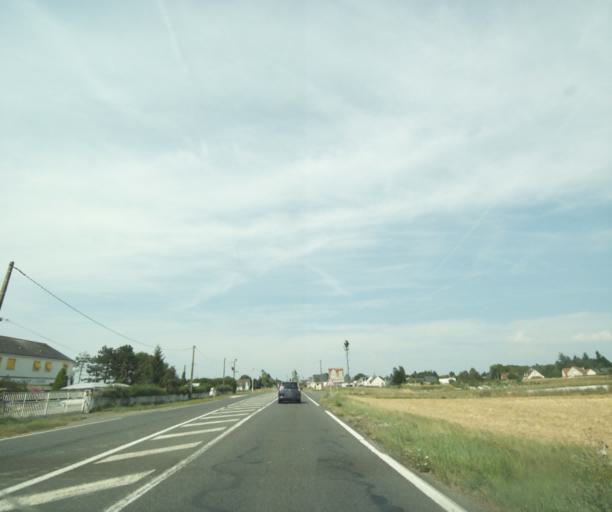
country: FR
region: Centre
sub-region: Departement d'Indre-et-Loire
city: Sorigny
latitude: 47.2358
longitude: 0.6906
